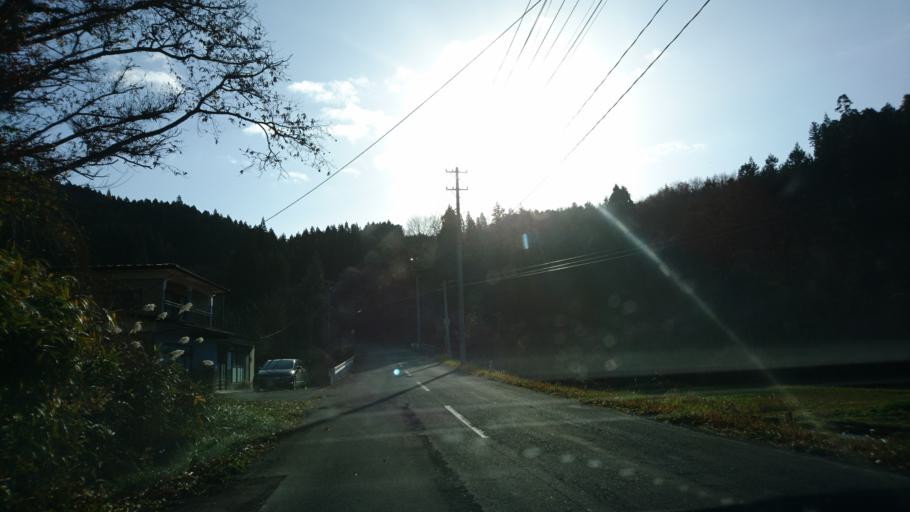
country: JP
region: Iwate
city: Ichinoseki
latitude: 38.8635
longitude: 141.3371
